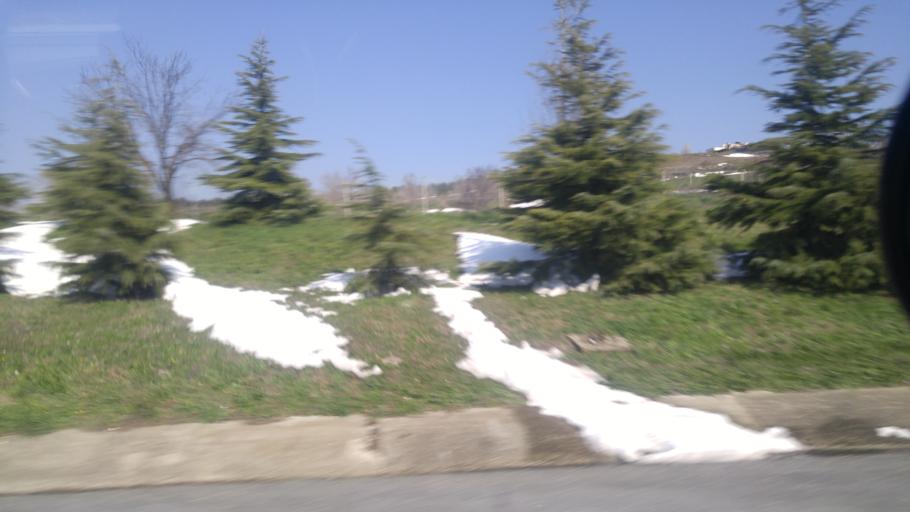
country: TR
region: Istanbul
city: Celaliye
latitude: 41.0605
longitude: 28.4104
